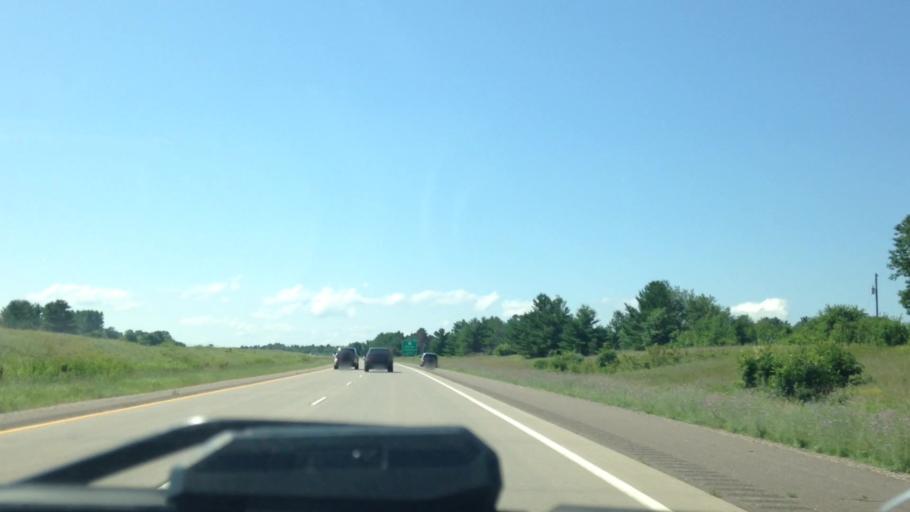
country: US
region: Wisconsin
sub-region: Barron County
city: Cameron
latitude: 45.4192
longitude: -91.7641
